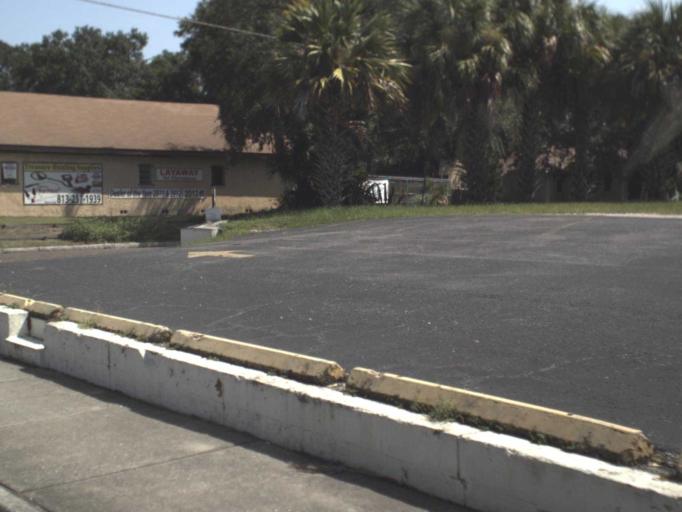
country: US
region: Florida
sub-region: Hillsborough County
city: Tampa
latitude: 27.9976
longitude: -82.4594
